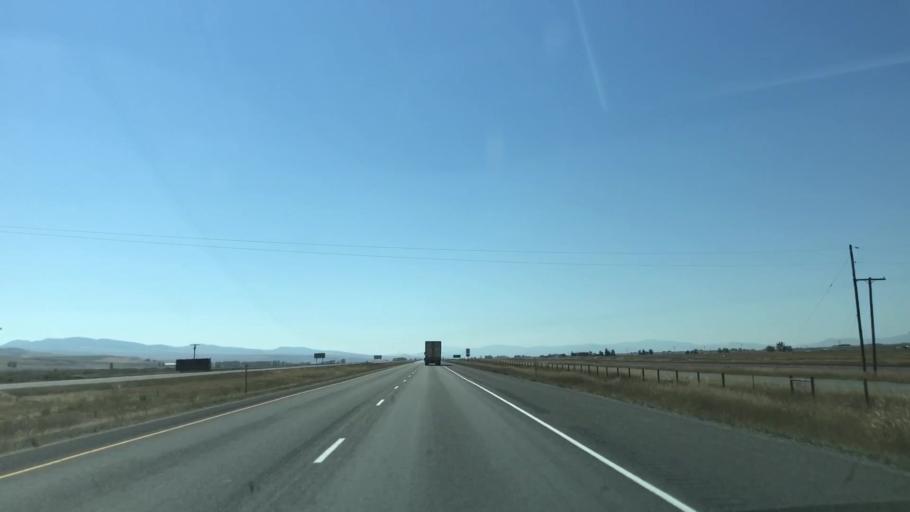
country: US
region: Montana
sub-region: Powell County
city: Deer Lodge
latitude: 46.3672
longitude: -112.7407
